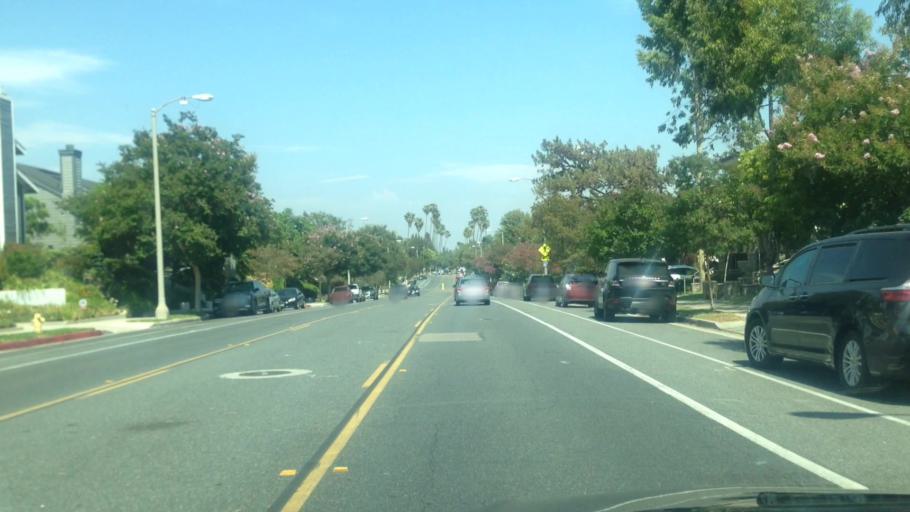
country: US
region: California
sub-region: Los Angeles County
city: South Pasadena
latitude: 34.1276
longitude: -118.1450
